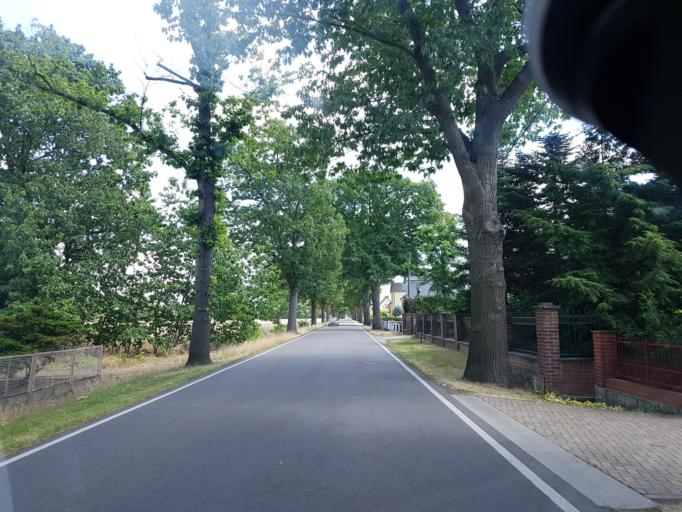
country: DE
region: Brandenburg
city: Cottbus
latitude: 51.7208
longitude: 14.3990
